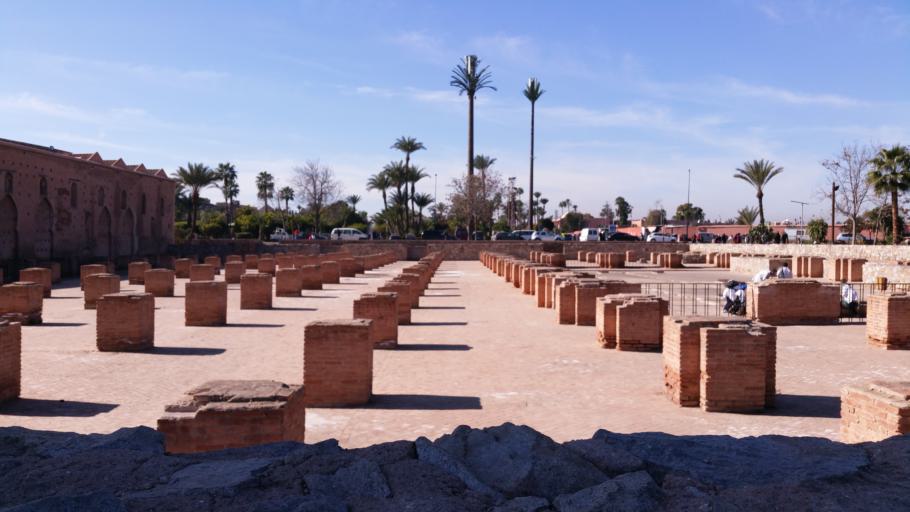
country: MA
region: Marrakech-Tensift-Al Haouz
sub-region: Marrakech
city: Marrakesh
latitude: 31.6244
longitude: -7.9934
